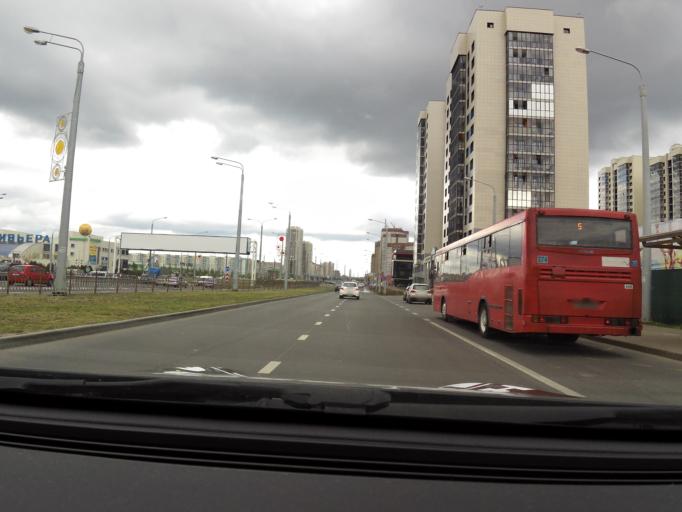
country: RU
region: Tatarstan
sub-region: Gorod Kazan'
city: Kazan
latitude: 55.8134
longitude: 49.1342
